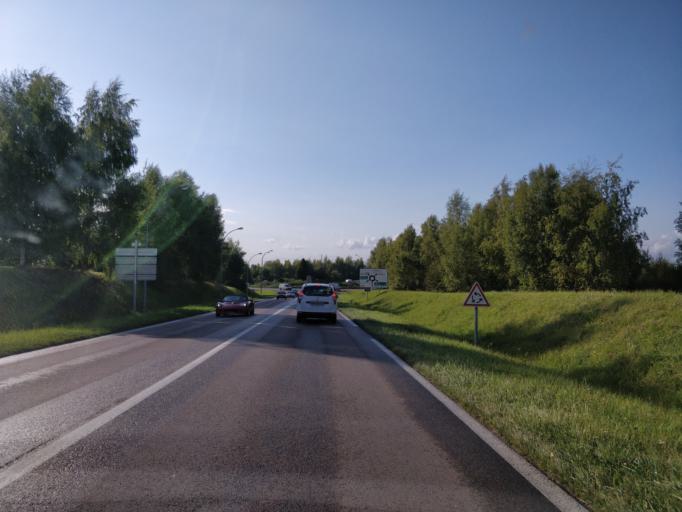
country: FR
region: Champagne-Ardenne
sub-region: Departement de l'Aube
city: Saint-Parres-aux-Tertres
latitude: 48.2952
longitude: 4.1402
